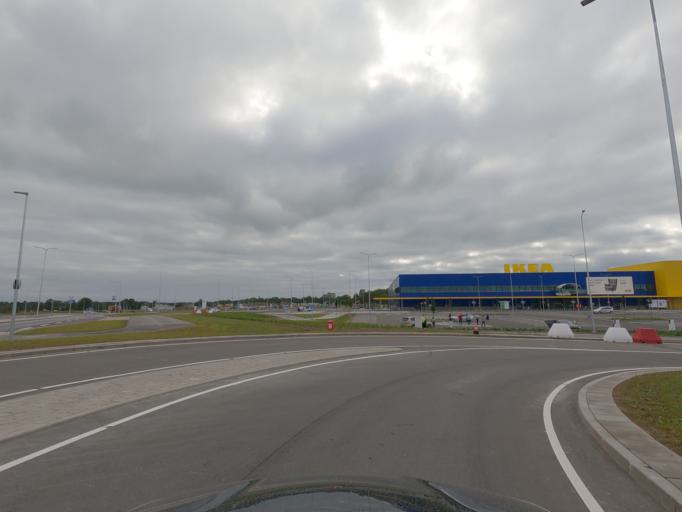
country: EE
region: Harju
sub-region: Kiili vald
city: Kiili
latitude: 59.3399
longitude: 24.8248
